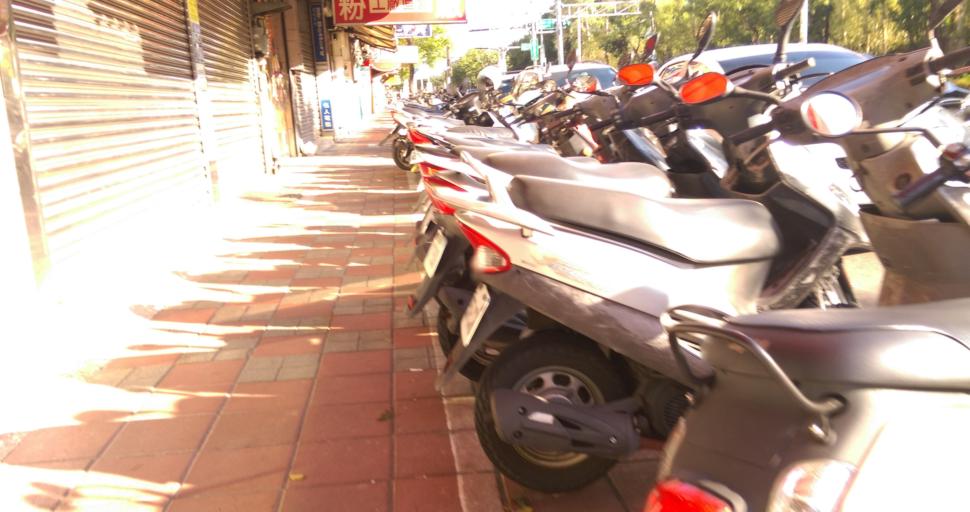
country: TW
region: Taiwan
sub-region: Hsinchu
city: Hsinchu
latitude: 24.7940
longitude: 121.0006
